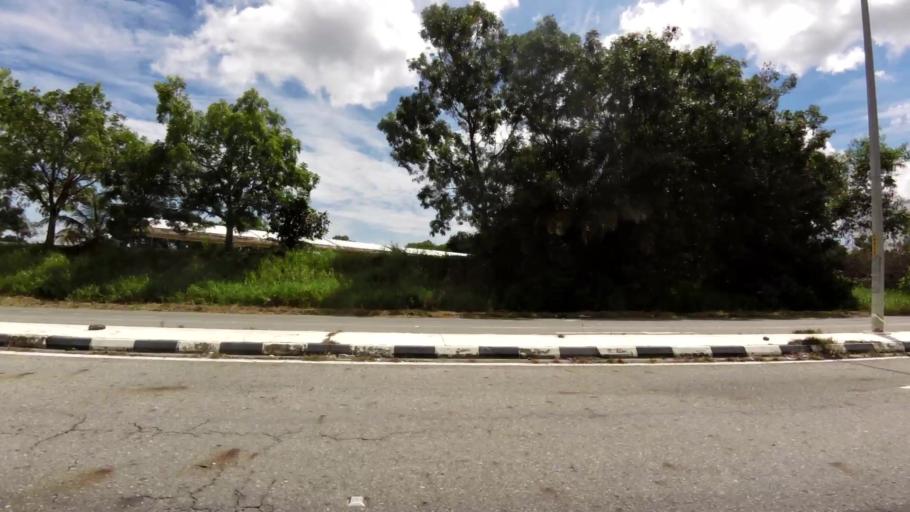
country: BN
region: Brunei and Muara
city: Bandar Seri Begawan
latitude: 4.9536
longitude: 114.9185
